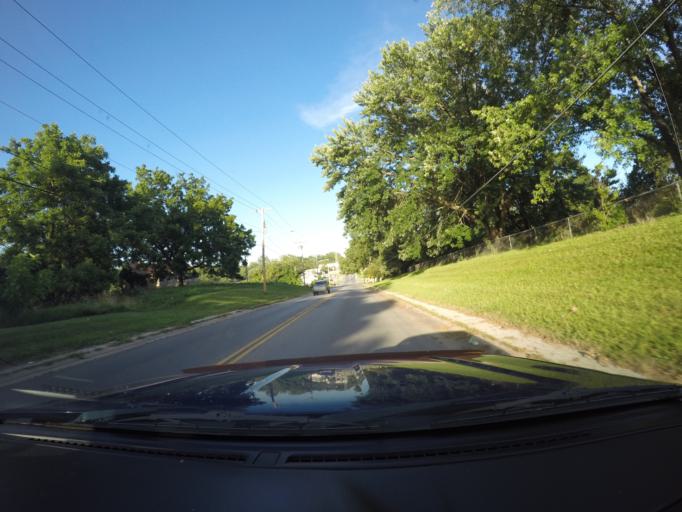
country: US
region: Kansas
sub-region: Wyandotte County
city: Edwardsville
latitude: 39.1431
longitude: -94.7684
